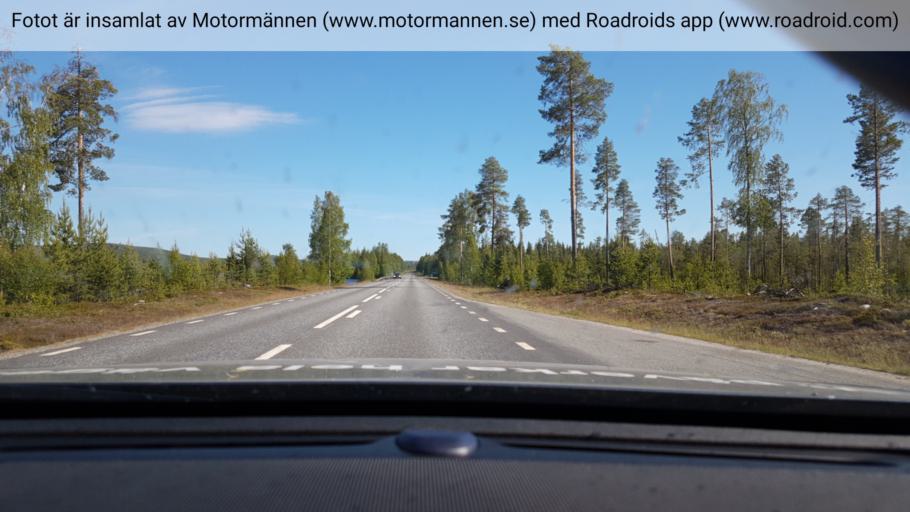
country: SE
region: Vaesterbotten
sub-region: Lycksele Kommun
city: Soderfors
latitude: 64.7496
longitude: 18.1858
